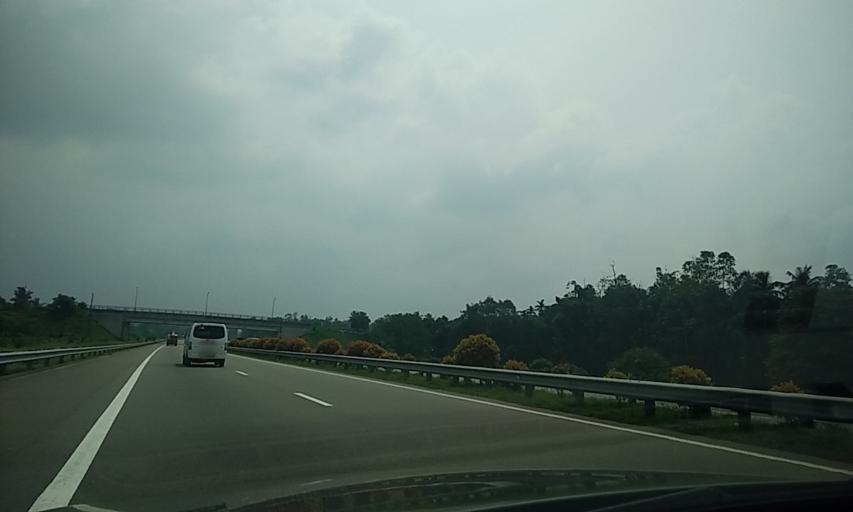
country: LK
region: Western
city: Homagama
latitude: 6.8760
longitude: 79.9777
